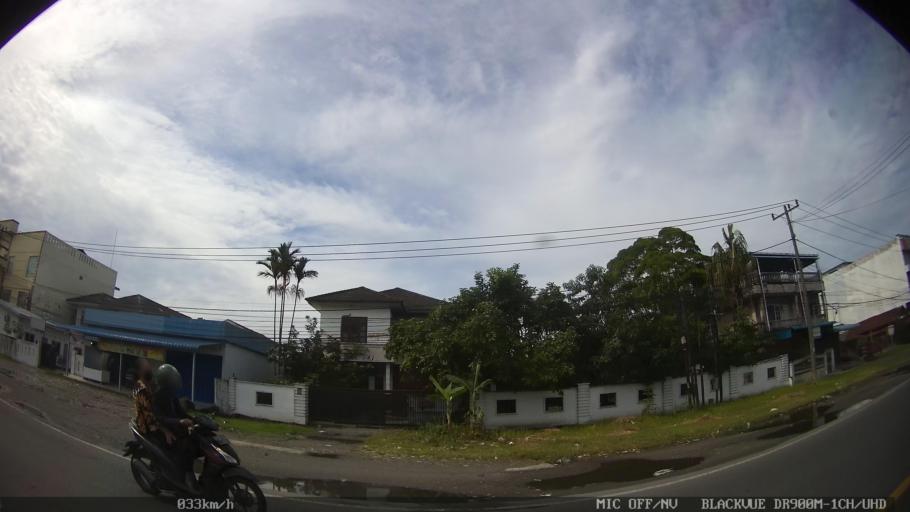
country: ID
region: North Sumatra
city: Medan
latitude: 3.6150
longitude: 98.6463
